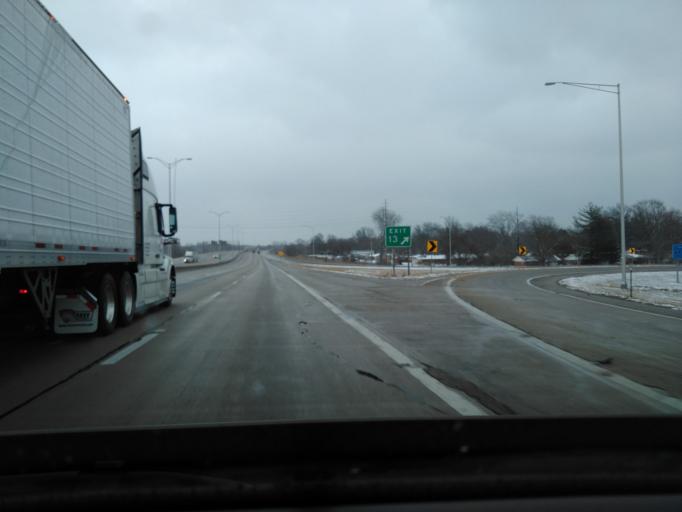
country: US
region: Illinois
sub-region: Saint Clair County
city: Cahokia
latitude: 38.5511
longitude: -90.1612
